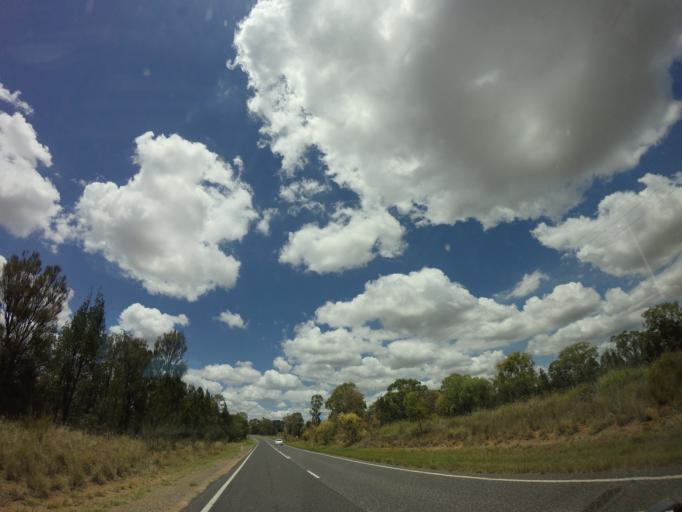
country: AU
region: Queensland
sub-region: Western Downs
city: Dalby
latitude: -27.9723
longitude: 151.1086
